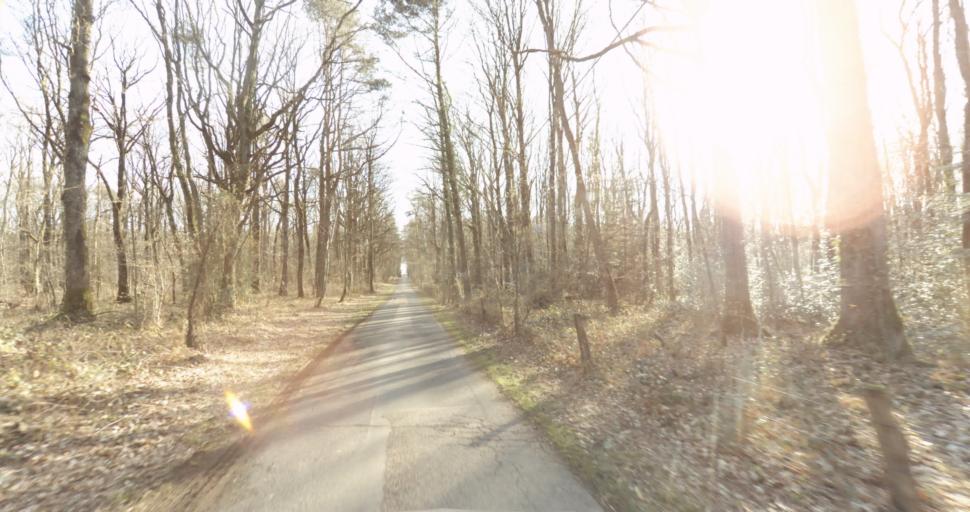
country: FR
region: Lower Normandy
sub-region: Departement du Calvados
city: Livarot
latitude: 48.9735
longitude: 0.0779
